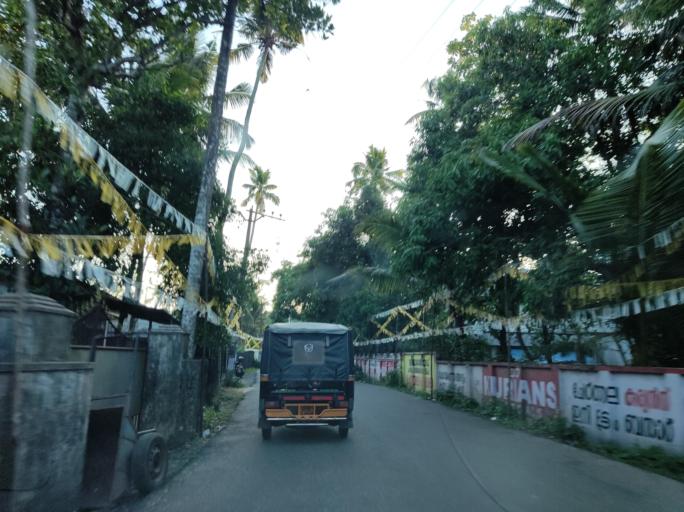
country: IN
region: Kerala
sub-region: Alappuzha
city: Vayalar
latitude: 9.7043
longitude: 76.3039
